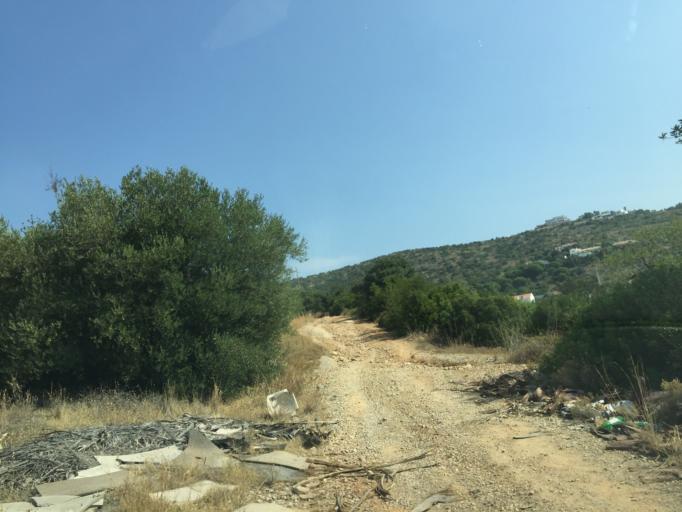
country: PT
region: Faro
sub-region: Loule
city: Almancil
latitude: 37.1047
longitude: -8.0051
